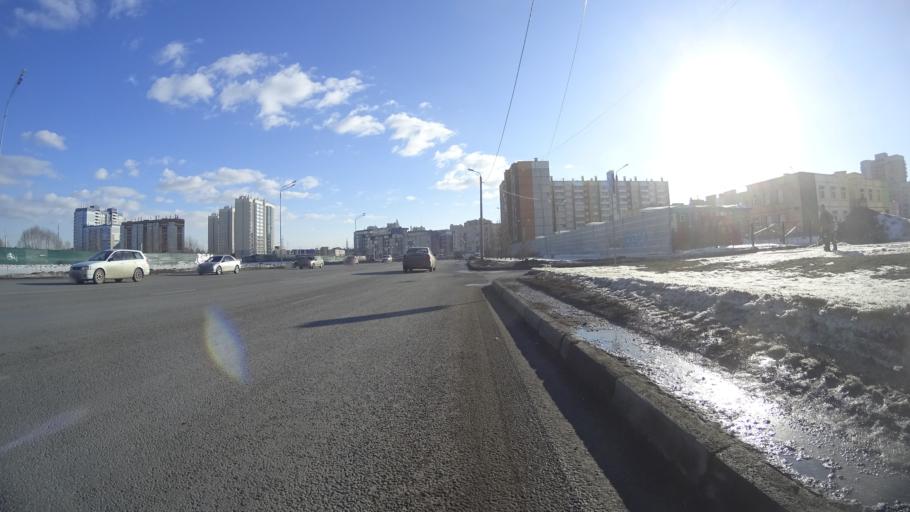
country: RU
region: Chelyabinsk
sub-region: Gorod Chelyabinsk
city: Chelyabinsk
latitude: 55.1619
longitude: 61.3023
